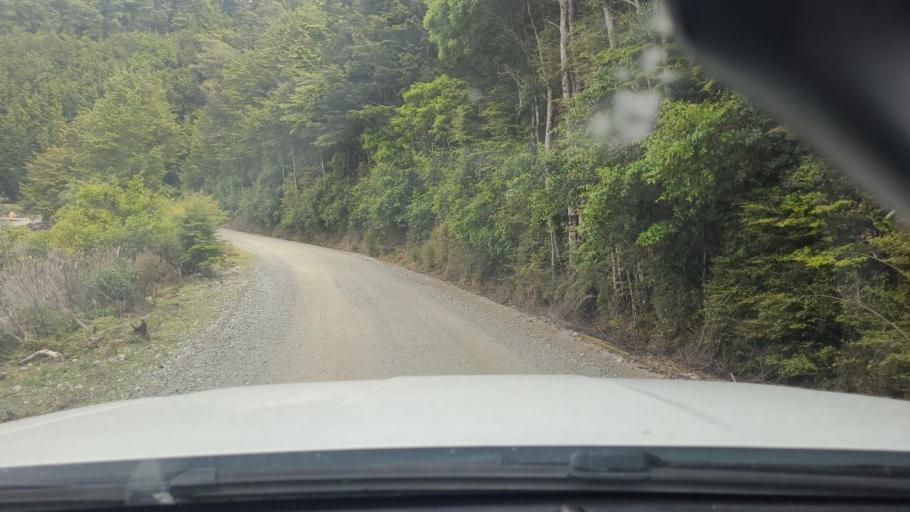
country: NZ
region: Southland
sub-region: Southland District
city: Te Anau
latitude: -45.5271
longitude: 167.6042
